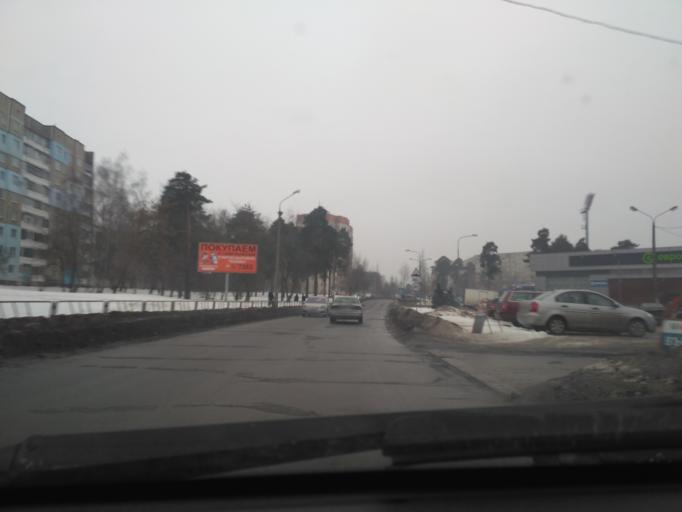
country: BY
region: Minsk
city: Horad Barysaw
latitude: 54.2203
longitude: 28.4900
